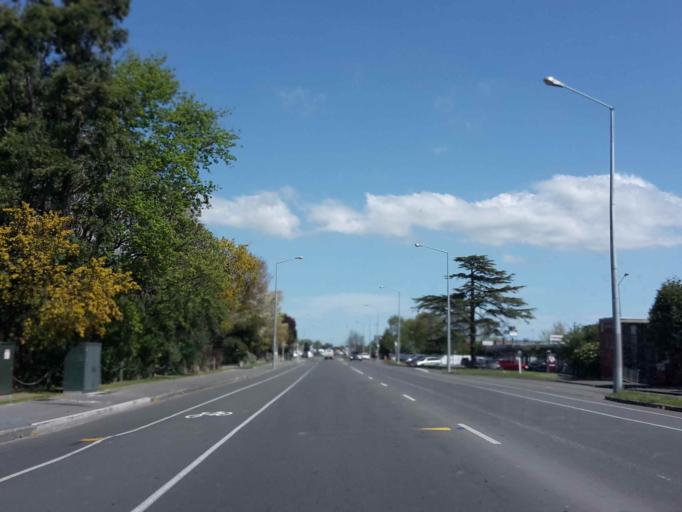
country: NZ
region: Canterbury
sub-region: Selwyn District
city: Prebbleton
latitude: -43.5378
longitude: 172.5566
